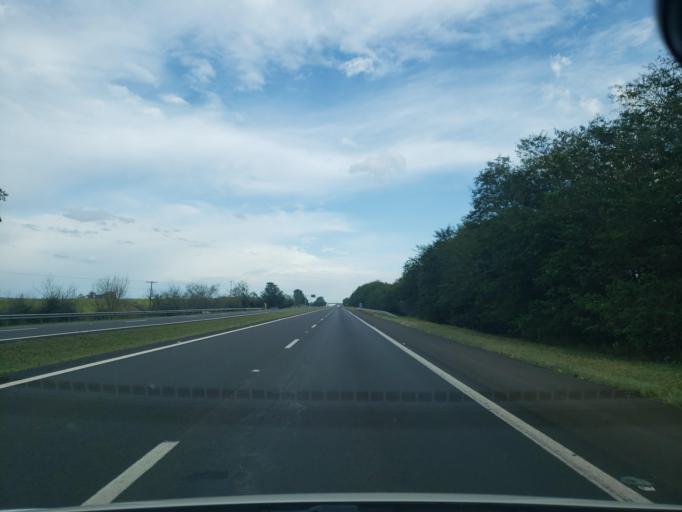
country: BR
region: Sao Paulo
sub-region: Itirapina
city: Itirapina
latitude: -22.2661
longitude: -47.9211
